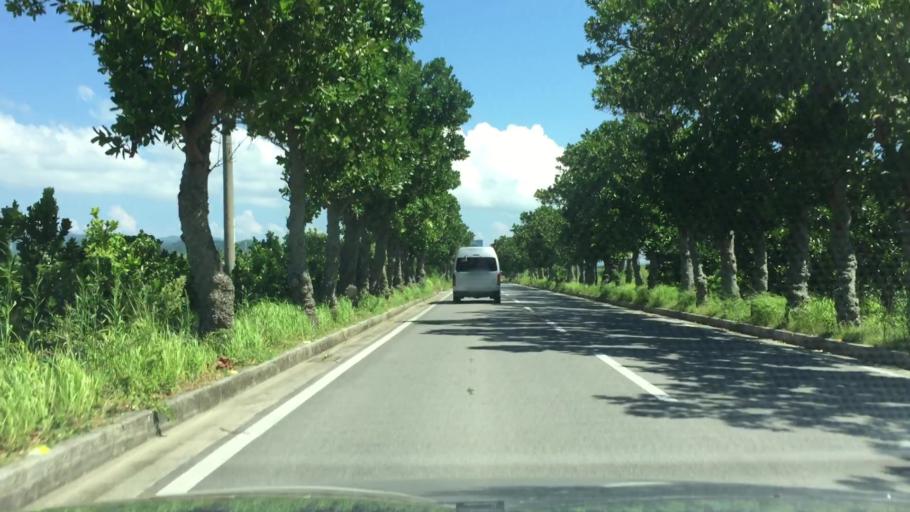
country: JP
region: Okinawa
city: Ishigaki
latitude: 24.3724
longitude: 124.2462
